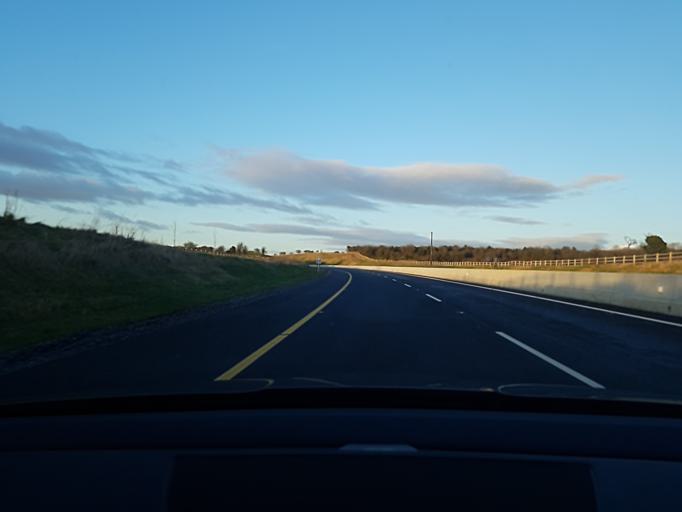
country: IE
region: Connaught
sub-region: County Galway
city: Athenry
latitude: 53.3610
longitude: -8.7889
